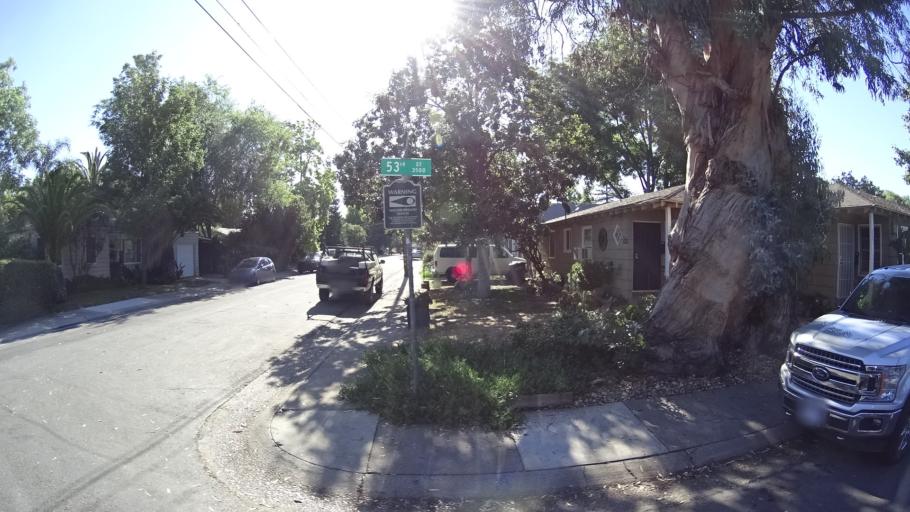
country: US
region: California
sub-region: Sacramento County
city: Parkway
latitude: 38.5426
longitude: -121.4440
